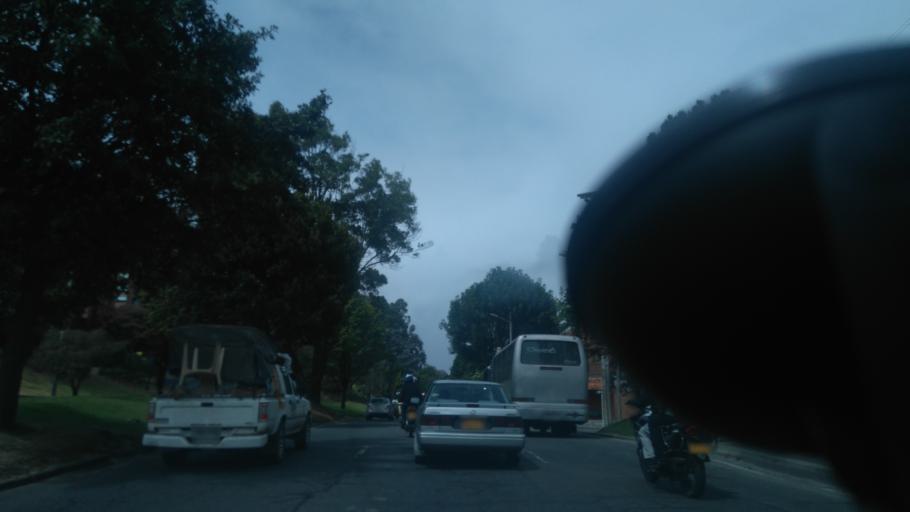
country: CO
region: Bogota D.C.
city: Barrio San Luis
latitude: 4.7198
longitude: -74.0275
